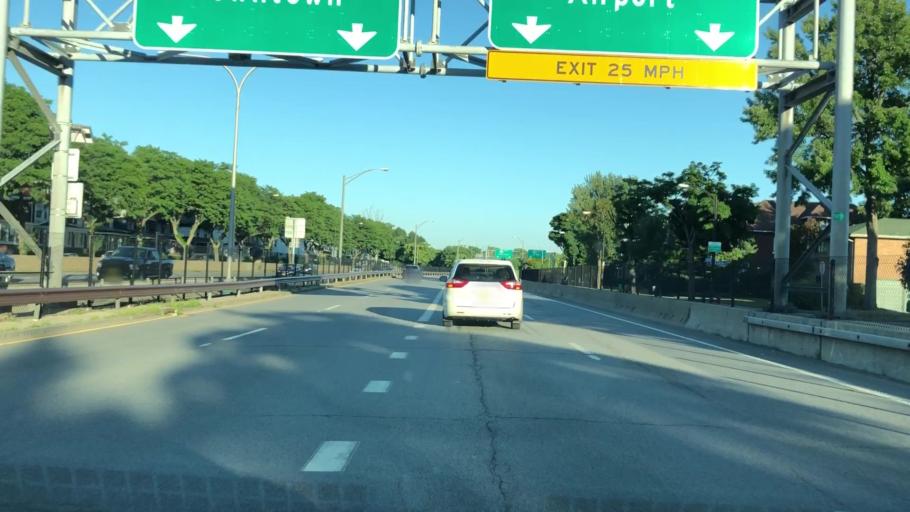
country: US
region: New York
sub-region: Erie County
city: Kenmore
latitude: 42.9258
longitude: -78.8477
